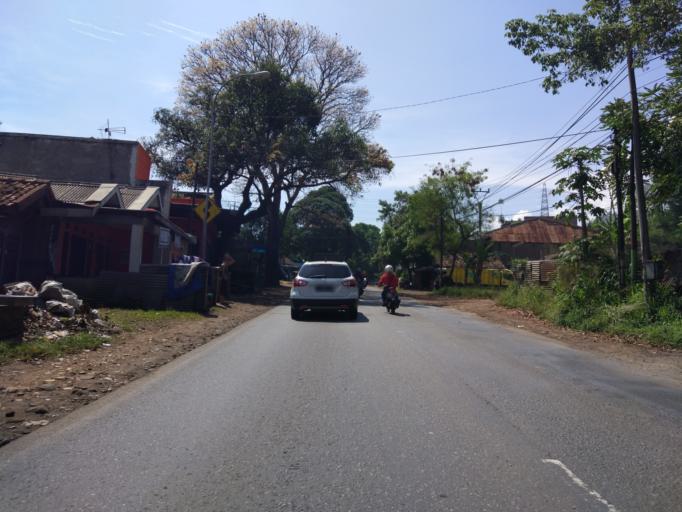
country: ID
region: West Java
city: Cileunyi
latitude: -6.9229
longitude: 107.7870
